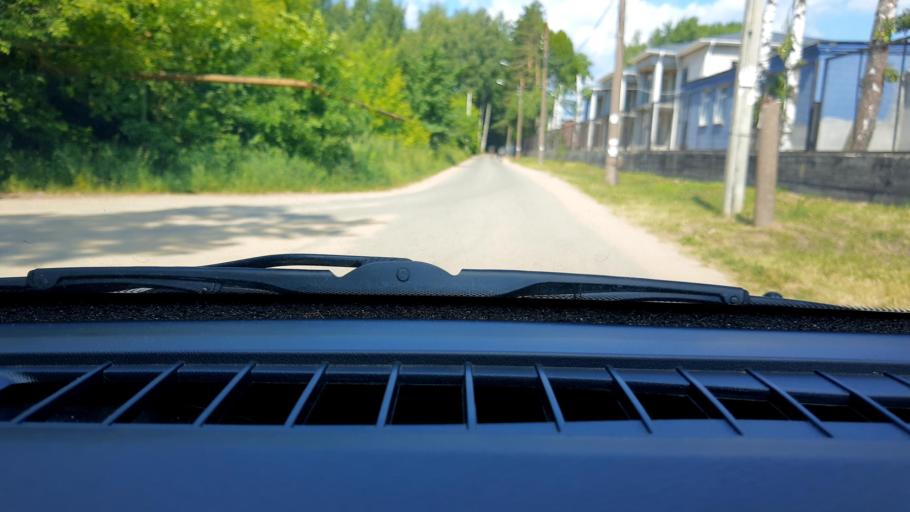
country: RU
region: Nizjnij Novgorod
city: Burevestnik
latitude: 56.1952
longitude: 43.7747
